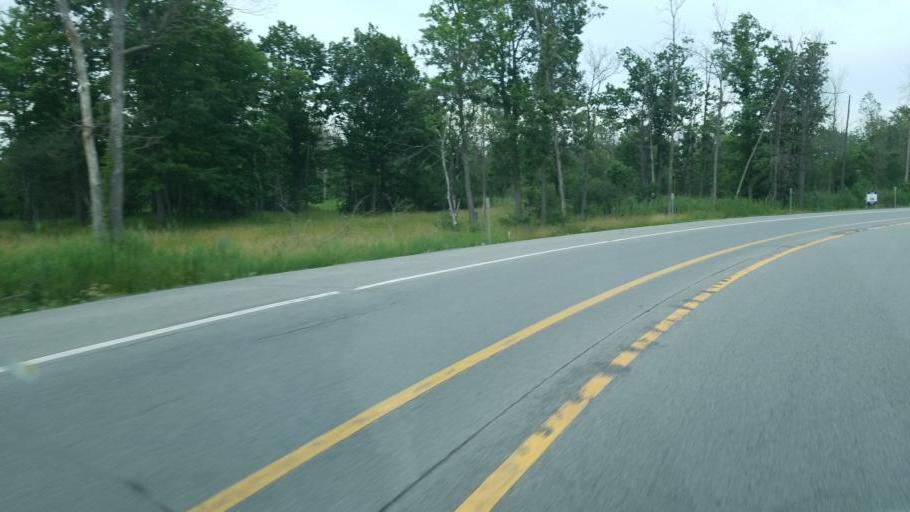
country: US
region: New York
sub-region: Erie County
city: Harris Hill
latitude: 42.9526
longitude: -78.7042
